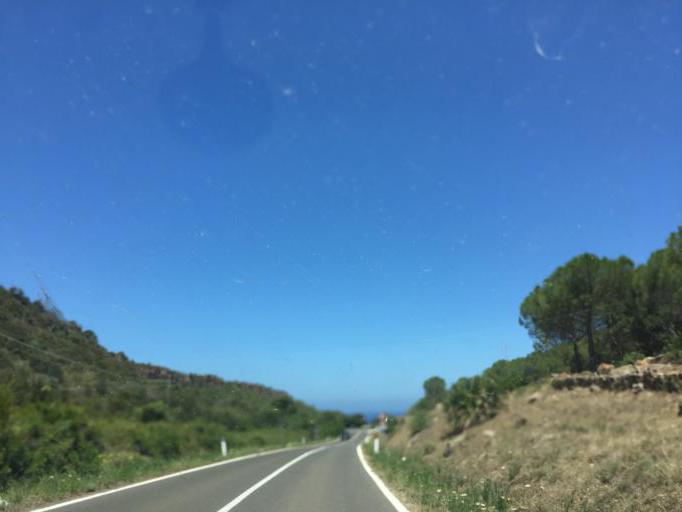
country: IT
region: Sardinia
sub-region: Provincia di Sassari
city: Castelsardo
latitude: 40.8985
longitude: 8.7426
